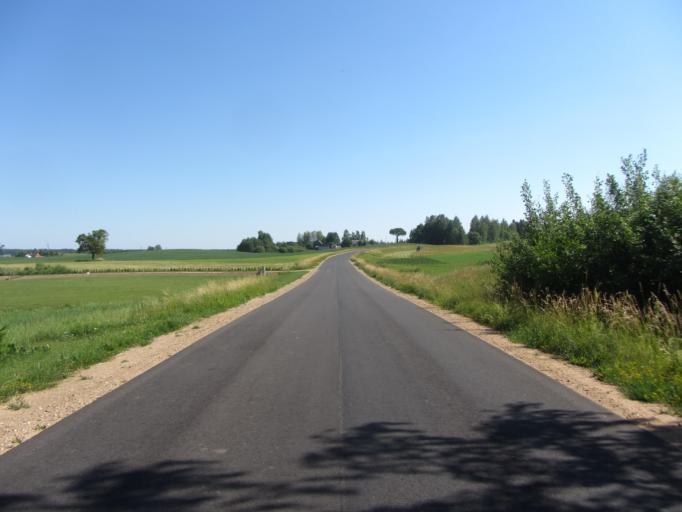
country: LT
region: Alytaus apskritis
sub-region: Alytus
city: Alytus
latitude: 54.3331
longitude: 24.1132
